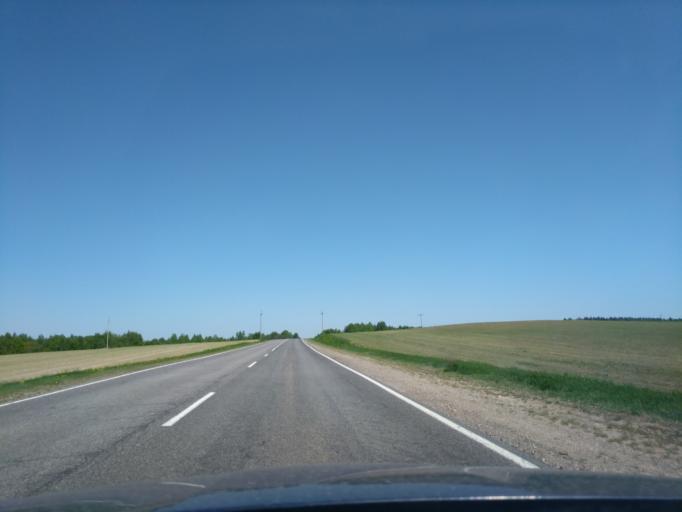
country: BY
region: Minsk
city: Il'ya
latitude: 54.3003
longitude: 27.4776
